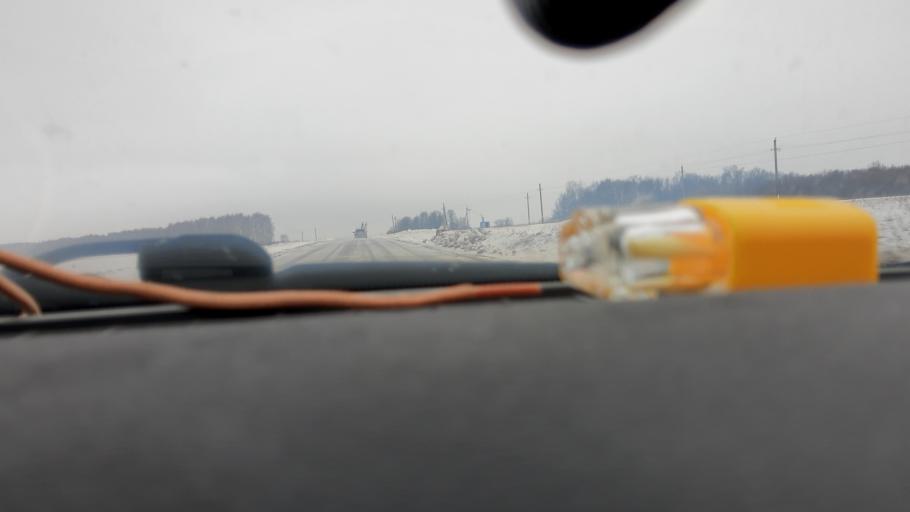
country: RU
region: Bashkortostan
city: Ulukulevo
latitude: 54.5882
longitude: 56.4260
